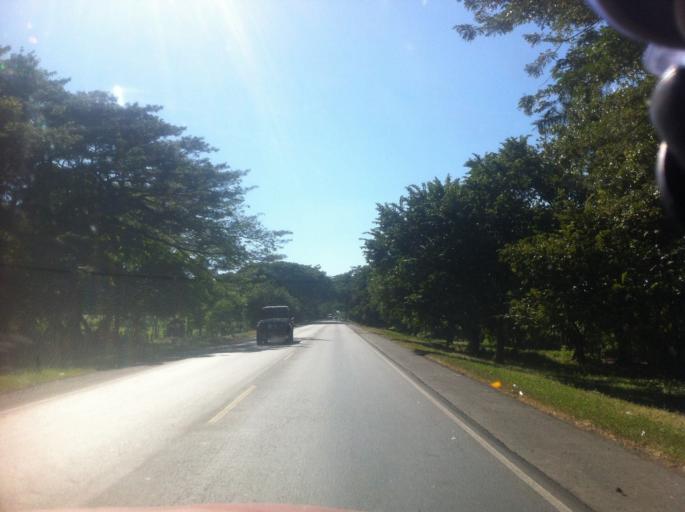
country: NI
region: Managua
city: Tipitapa
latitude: 12.1611
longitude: -86.1319
